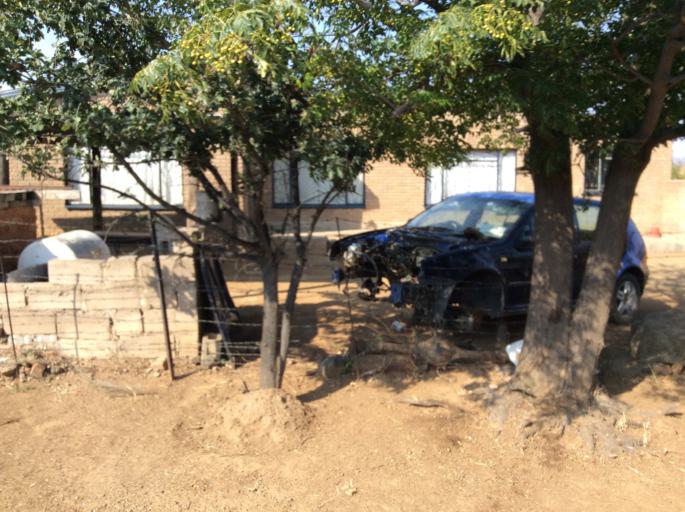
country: LS
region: Mafeteng
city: Mafeteng
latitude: -29.7156
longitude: 27.0296
